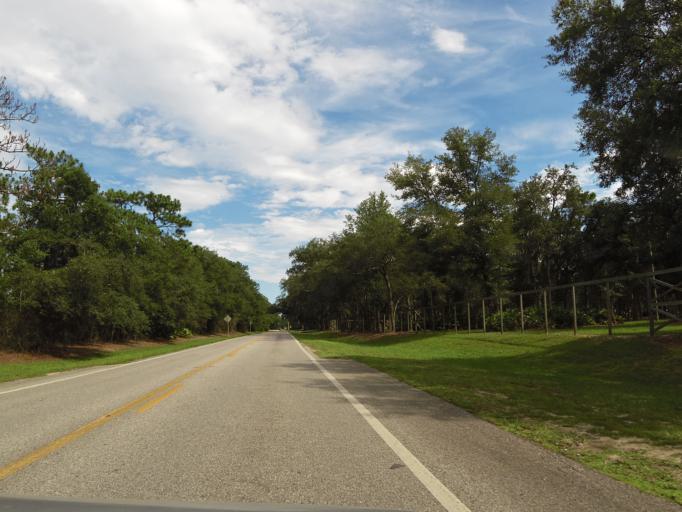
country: US
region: Florida
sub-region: Clay County
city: Green Cove Springs
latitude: 30.0326
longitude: -81.7225
